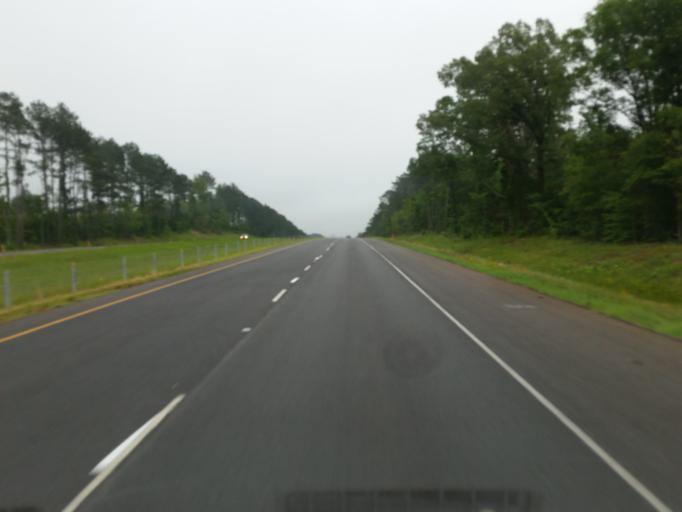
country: US
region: Louisiana
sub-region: Bienville Parish
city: Arcadia
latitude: 32.5633
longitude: -93.0740
